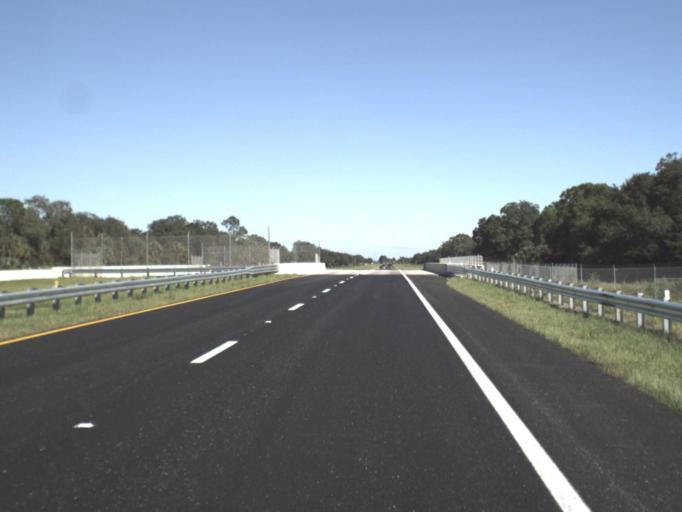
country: US
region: Florida
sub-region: Hendry County
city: Port LaBelle
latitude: 26.7683
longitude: -81.3253
